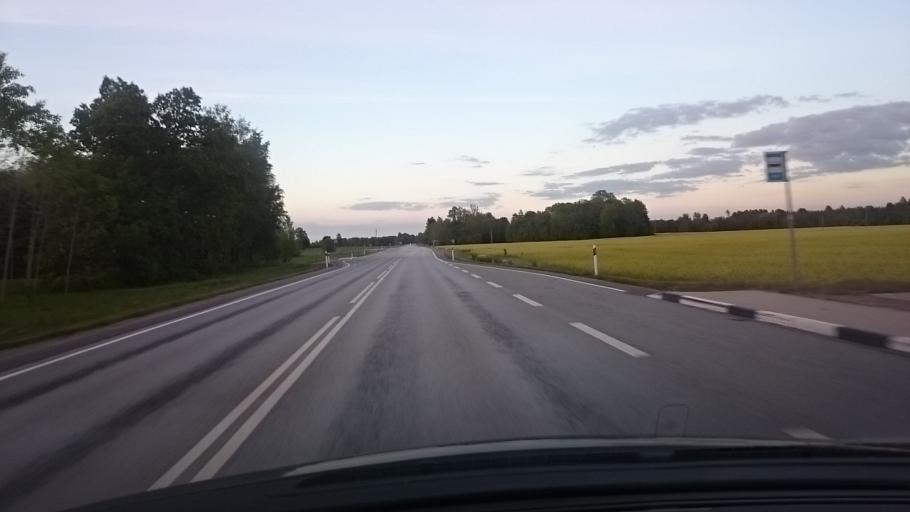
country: EE
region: Viljandimaa
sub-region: Vohma linn
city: Vohma
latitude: 58.6571
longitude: 25.6056
